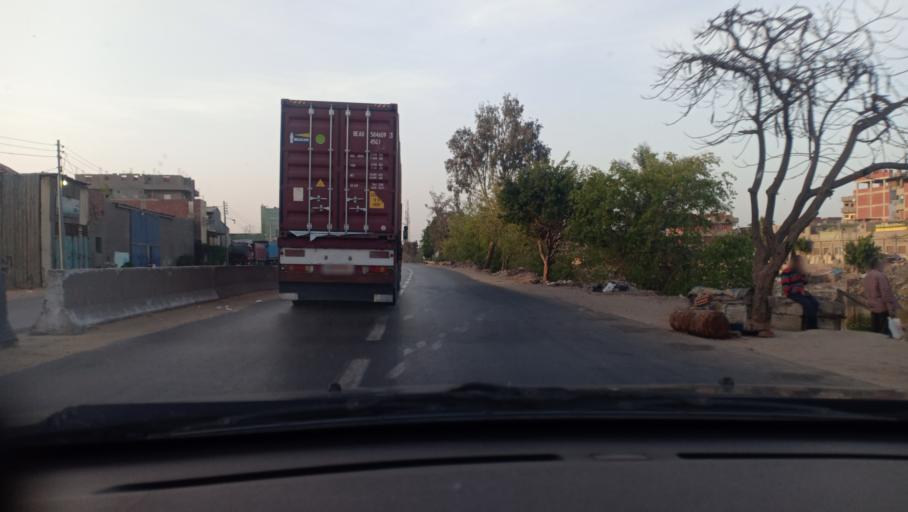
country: EG
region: Muhafazat al Gharbiyah
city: Zifta
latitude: 30.6415
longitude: 31.2817
